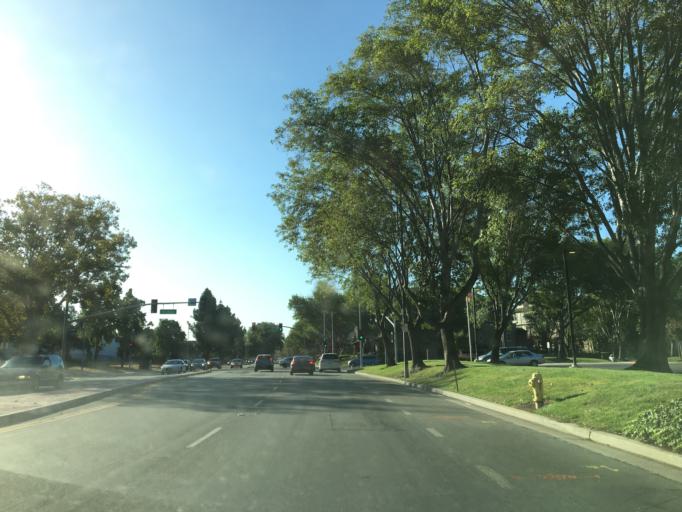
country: US
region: California
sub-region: Santa Clara County
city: Milpitas
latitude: 37.3922
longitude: -121.8903
